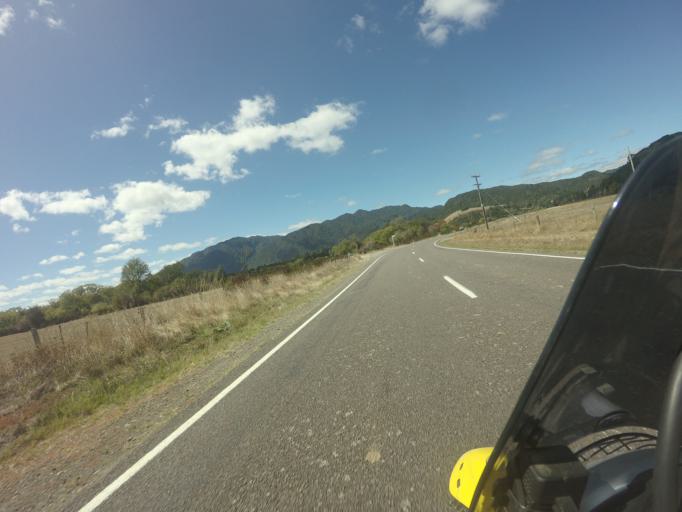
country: NZ
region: Bay of Plenty
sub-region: Whakatane District
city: Murupara
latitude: -38.4713
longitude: 176.7350
